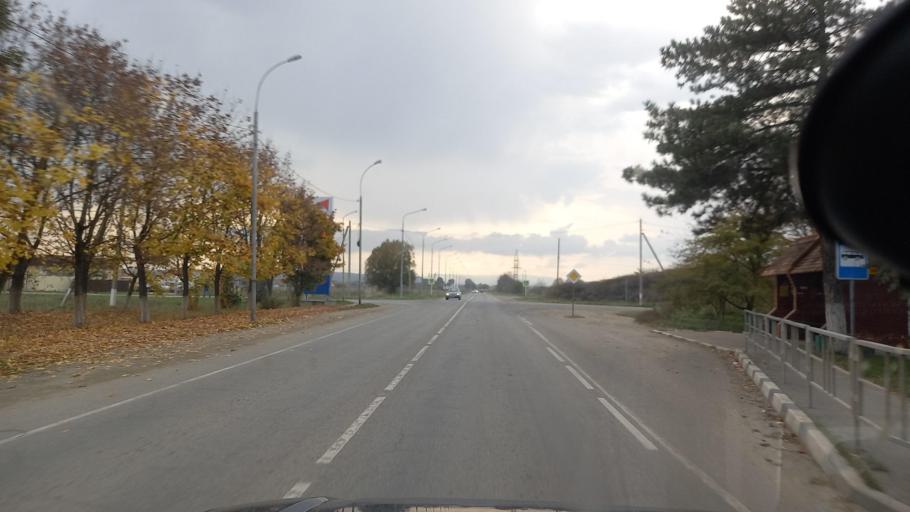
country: RU
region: Krasnodarskiy
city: Mostovskoy
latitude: 44.4026
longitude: 40.7821
